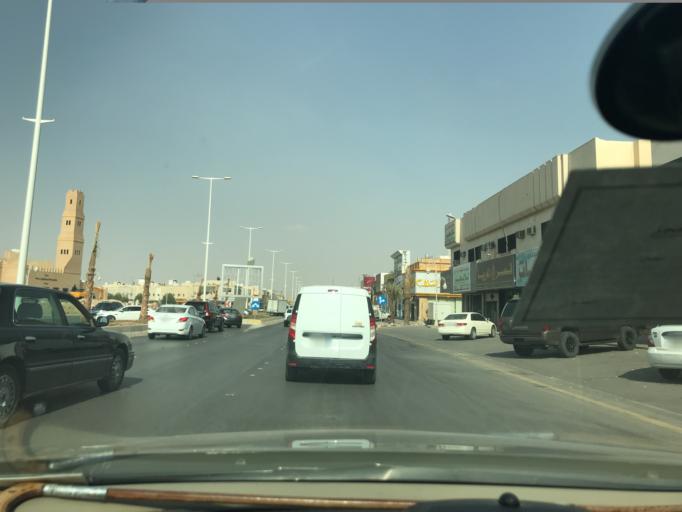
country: SA
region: Ar Riyad
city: Riyadh
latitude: 24.7450
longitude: 46.7570
